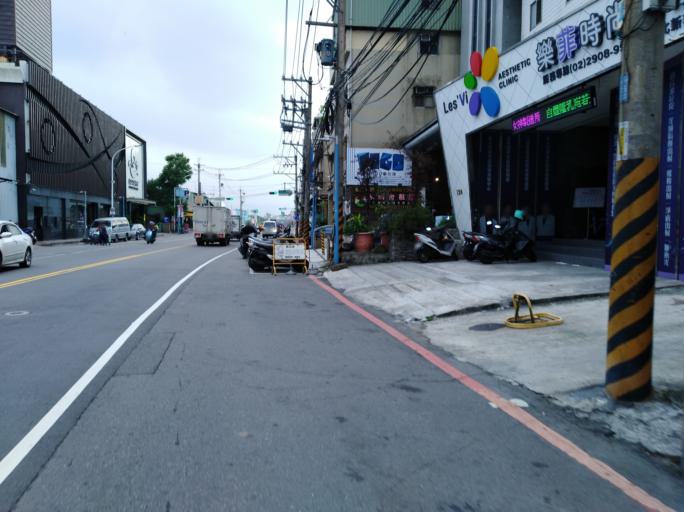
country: TW
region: Taipei
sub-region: Taipei
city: Banqiao
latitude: 25.0292
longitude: 121.4348
